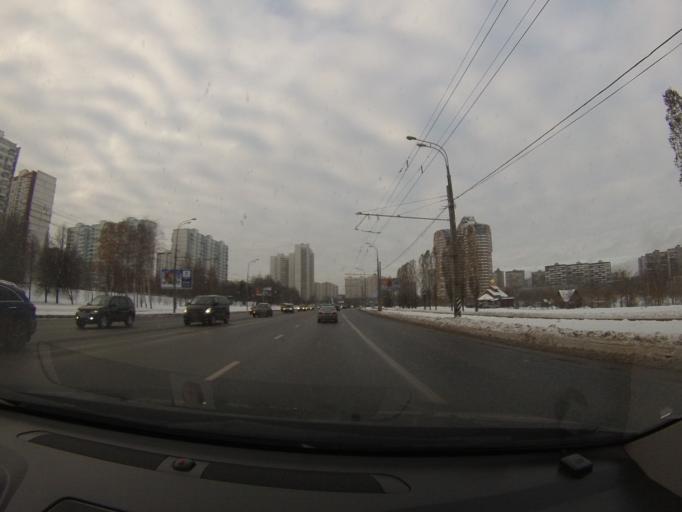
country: RU
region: Moscow
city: Nikulino
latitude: 55.6750
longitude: 37.4607
